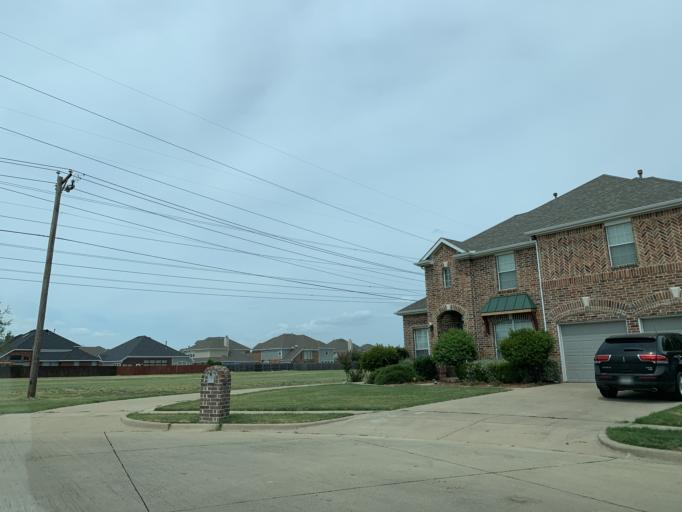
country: US
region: Texas
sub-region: Dallas County
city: Grand Prairie
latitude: 32.6541
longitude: -97.0387
